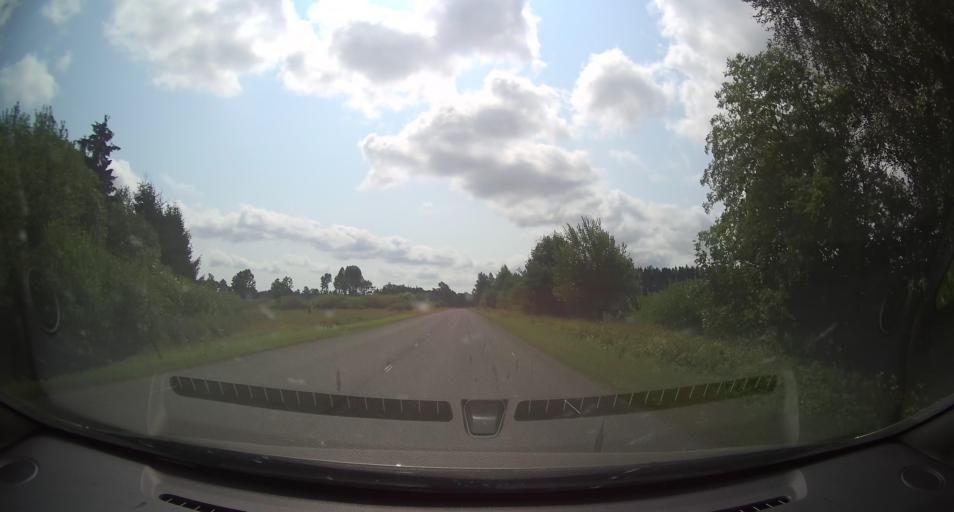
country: EE
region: Paernumaa
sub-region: Audru vald
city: Audru
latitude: 58.4910
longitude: 24.3357
